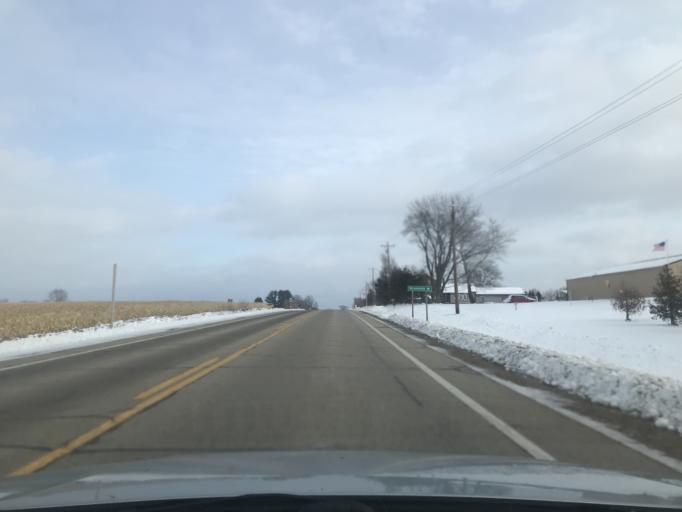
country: US
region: Wisconsin
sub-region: Oconto County
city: Oconto
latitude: 44.8929
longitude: -87.9715
